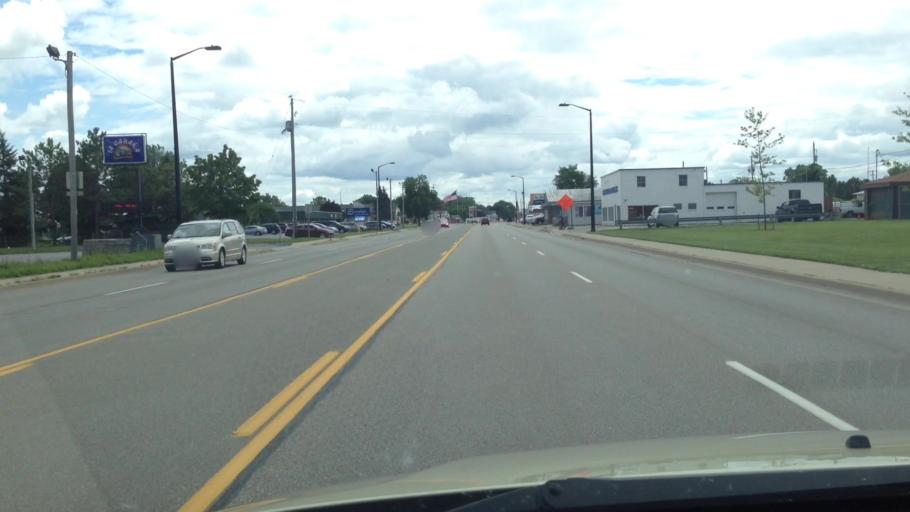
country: US
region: Michigan
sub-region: Menominee County
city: Menominee
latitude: 45.1249
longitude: -87.6131
